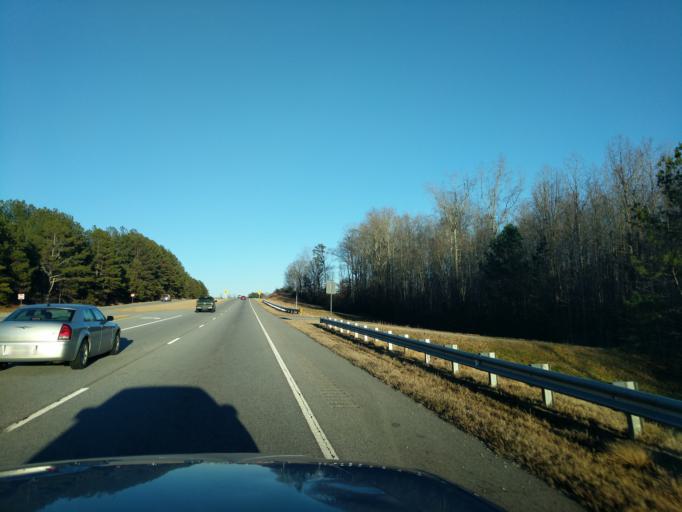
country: US
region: Georgia
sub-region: Stephens County
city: Toccoa
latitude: 34.5419
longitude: -83.2914
